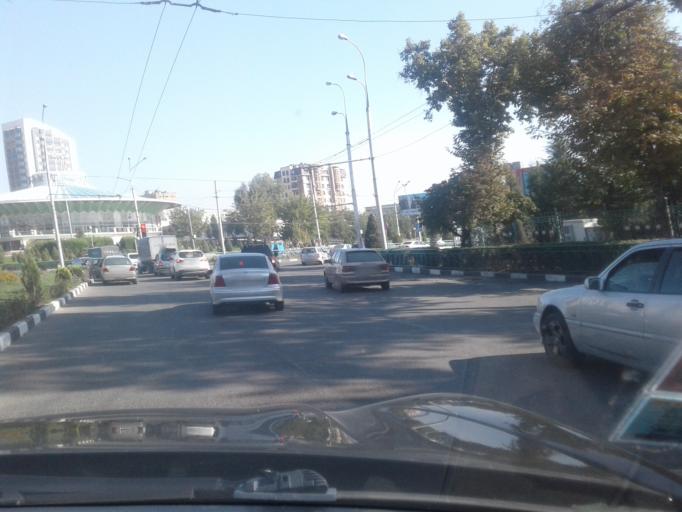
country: TJ
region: Dushanbe
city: Dushanbe
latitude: 38.5583
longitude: 68.7613
